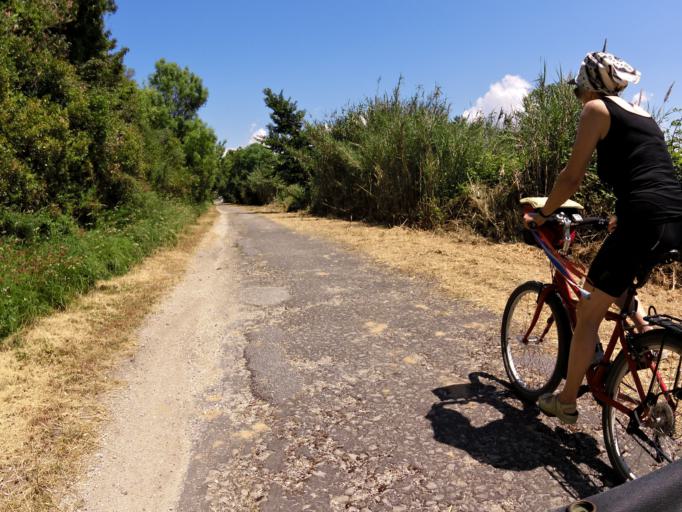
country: PT
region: Coimbra
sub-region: Montemor-O-Velho
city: Montemor-o-Velho
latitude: 40.1745
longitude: -8.6982
